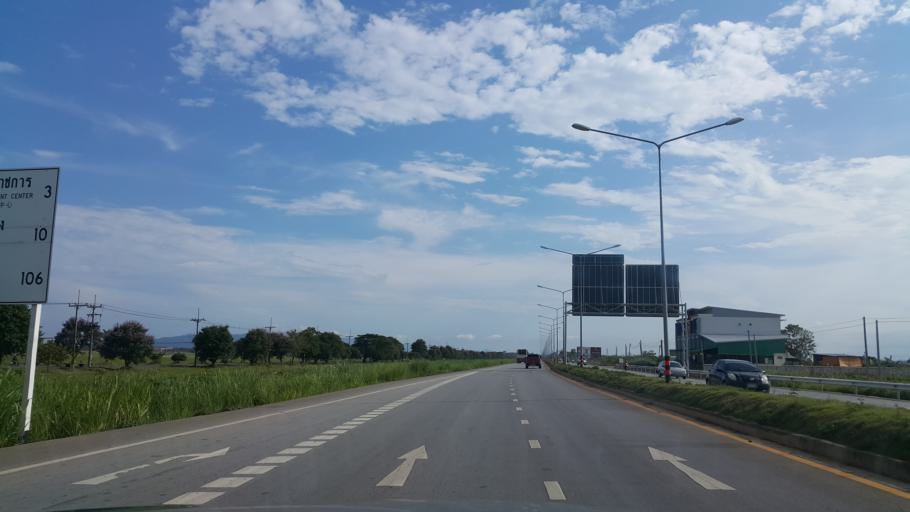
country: TH
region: Chiang Rai
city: Chiang Rai
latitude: 19.9515
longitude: 99.8751
